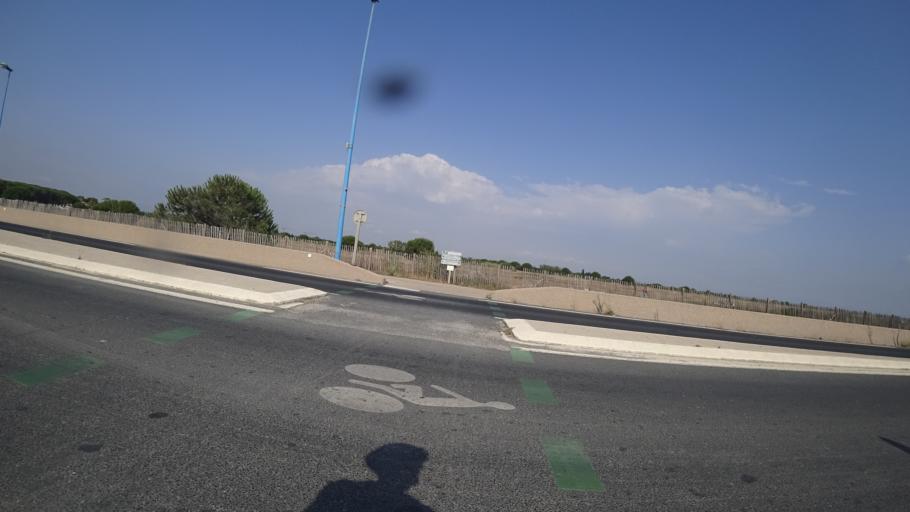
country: FR
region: Languedoc-Roussillon
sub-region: Departement des Pyrenees-Orientales
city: Saint-Cyprien-Plage
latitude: 42.6411
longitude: 3.0330
